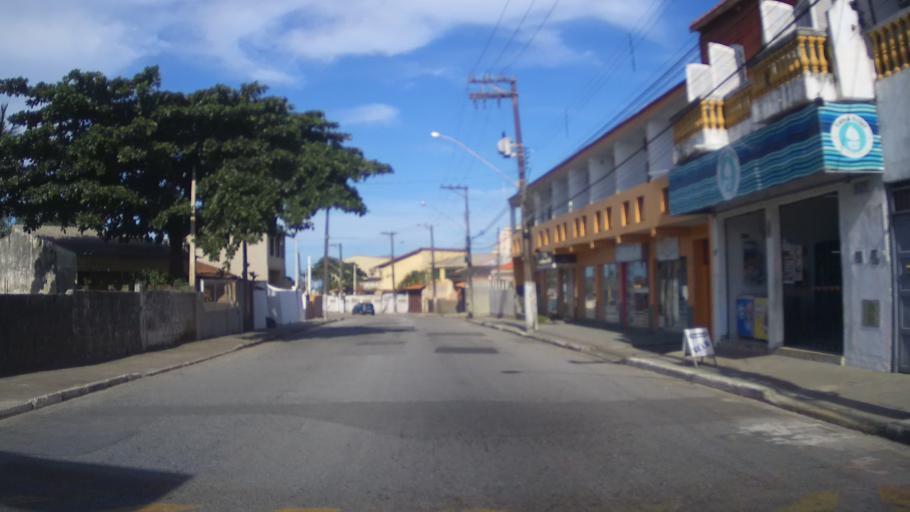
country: BR
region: Sao Paulo
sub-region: Itanhaem
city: Itanhaem
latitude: -24.1955
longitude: -46.8032
